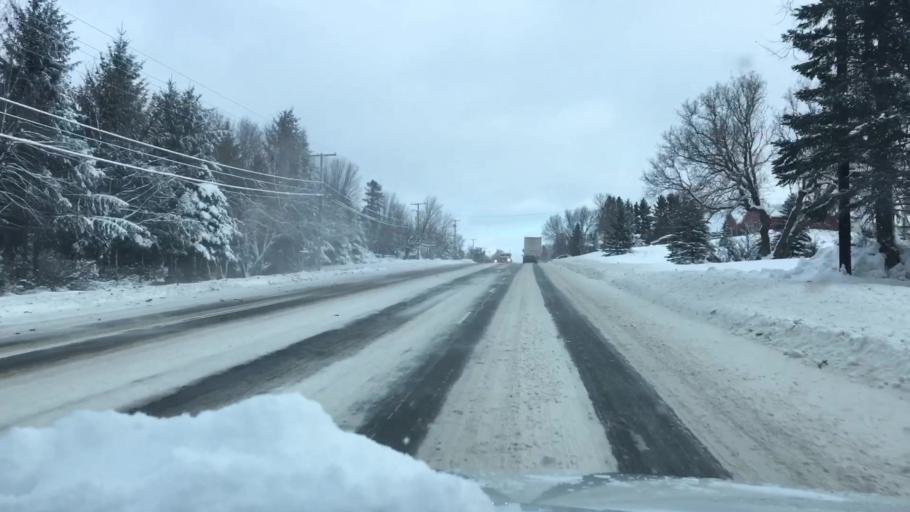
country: US
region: Maine
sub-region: Aroostook County
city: Presque Isle
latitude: 46.7236
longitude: -68.0052
